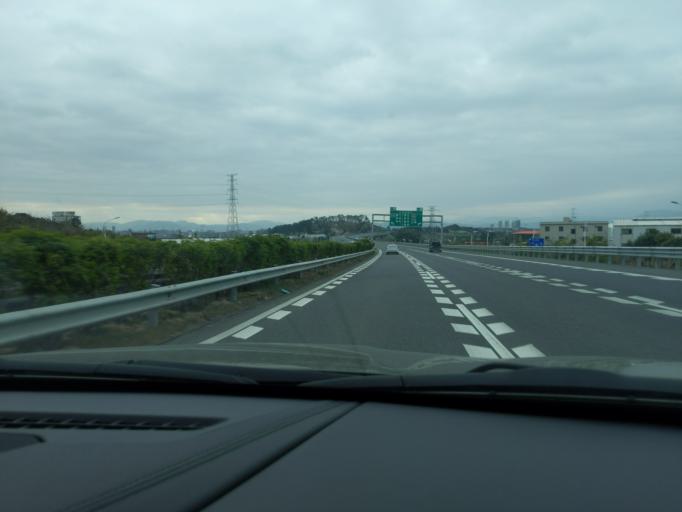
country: CN
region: Fujian
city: Neikeng
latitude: 24.7839
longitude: 118.4959
